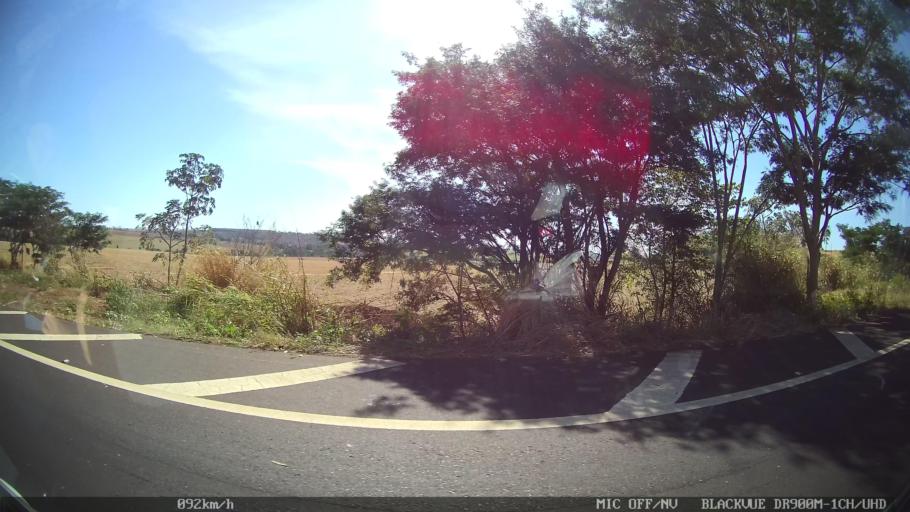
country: BR
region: Sao Paulo
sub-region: Barretos
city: Barretos
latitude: -20.6053
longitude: -48.7388
